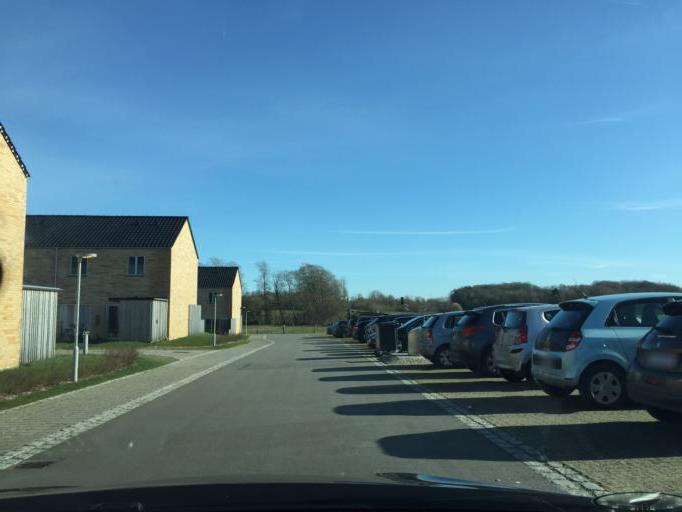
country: DK
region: South Denmark
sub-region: Odense Kommune
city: Hojby
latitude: 55.3416
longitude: 10.4211
